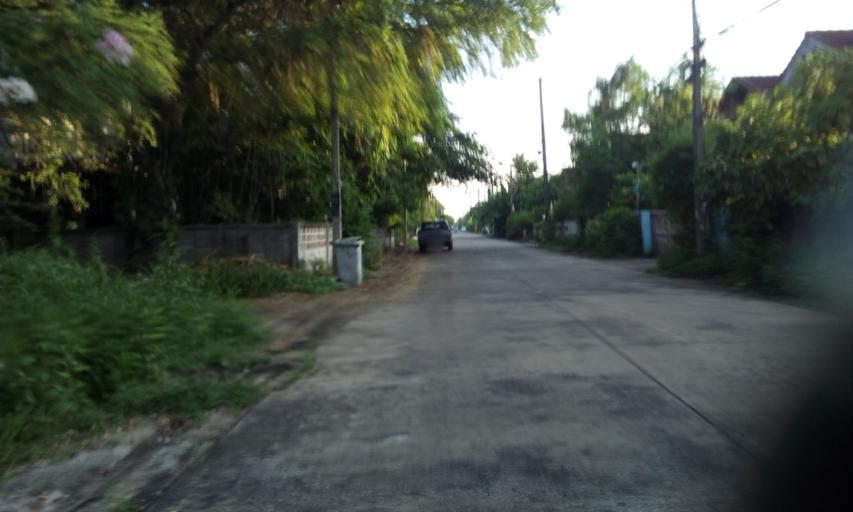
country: TH
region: Pathum Thani
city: Ban Rangsit
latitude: 14.0465
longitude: 100.8223
